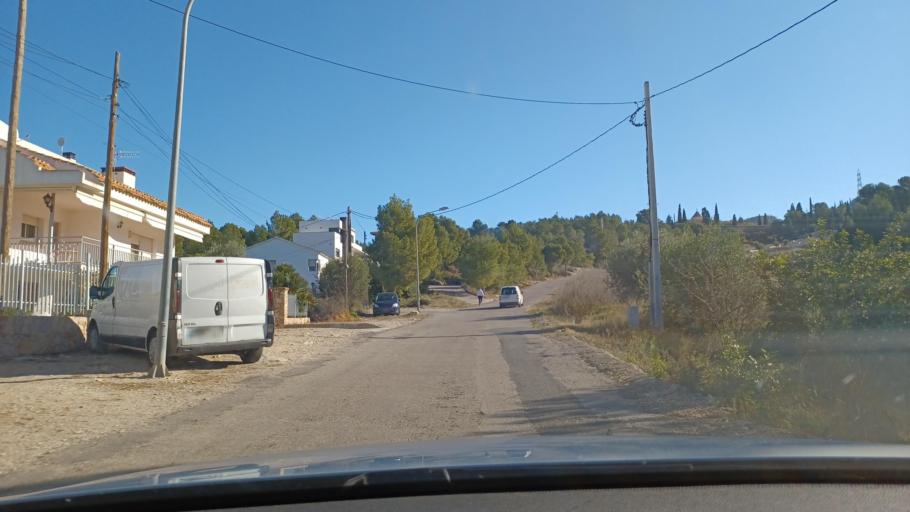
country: ES
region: Catalonia
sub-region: Provincia de Tarragona
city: Tortosa
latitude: 40.8139
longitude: 0.5468
